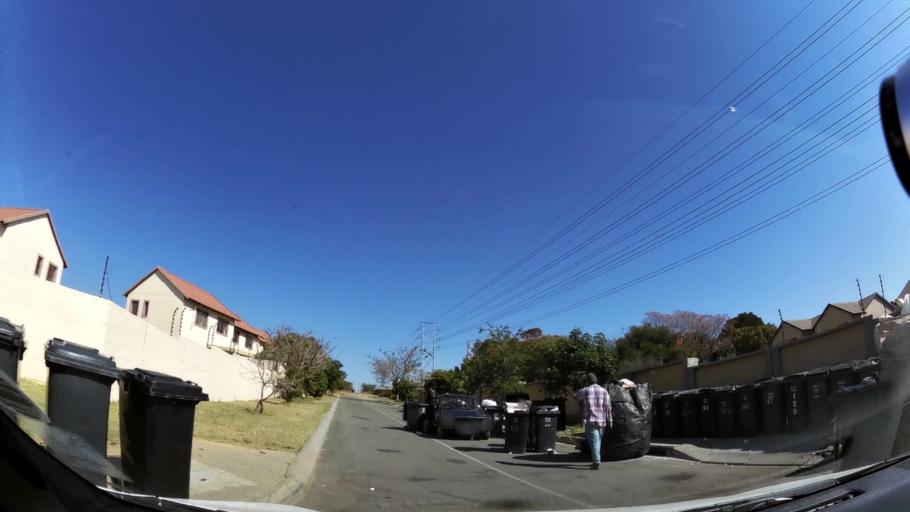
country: ZA
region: Gauteng
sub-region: City of Johannesburg Metropolitan Municipality
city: Midrand
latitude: -25.9683
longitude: 28.1051
